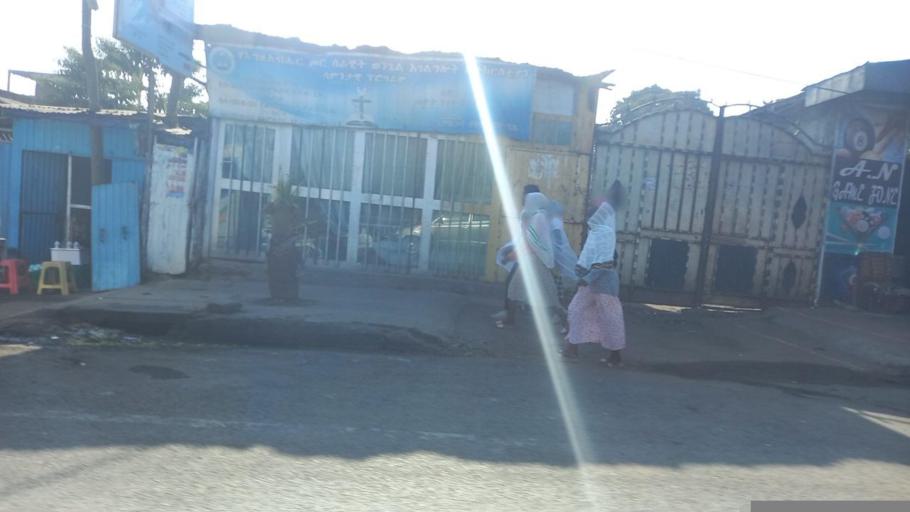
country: ET
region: Adis Abeba
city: Addis Ababa
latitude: 8.9384
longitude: 38.7473
